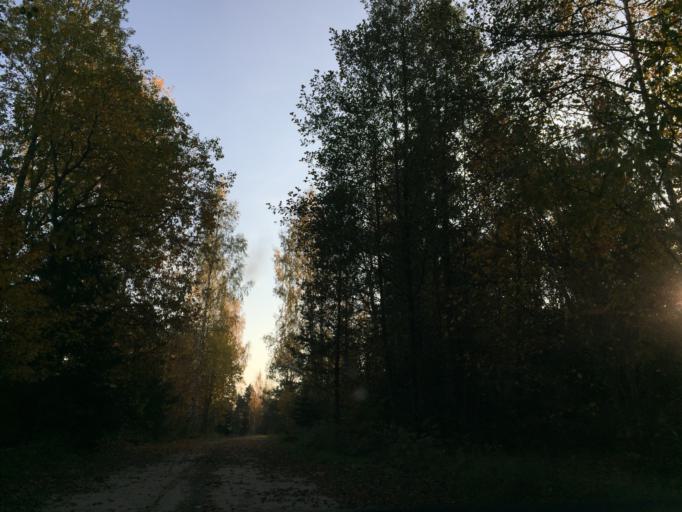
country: LV
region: Vainode
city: Vainode
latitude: 56.5882
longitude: 21.8325
